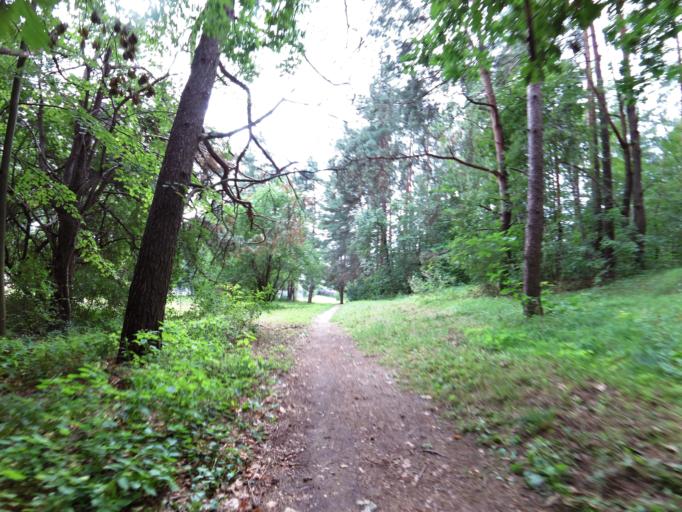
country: LT
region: Vilnius County
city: Lazdynai
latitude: 54.6784
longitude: 25.2073
